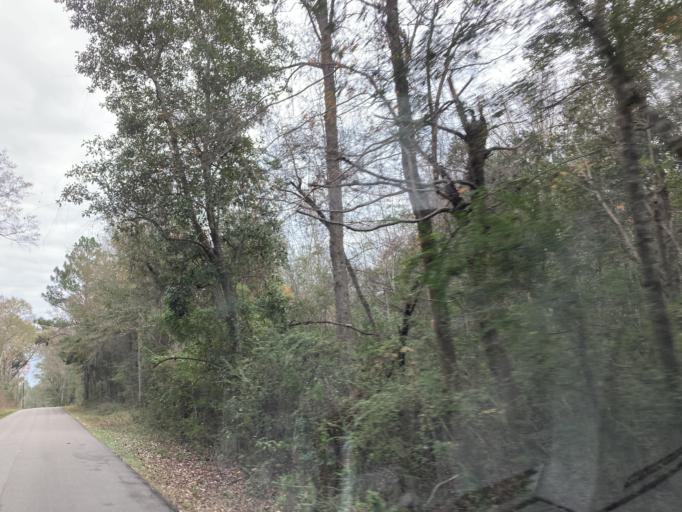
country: US
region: Mississippi
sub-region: Perry County
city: New Augusta
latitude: 31.0654
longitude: -89.1954
